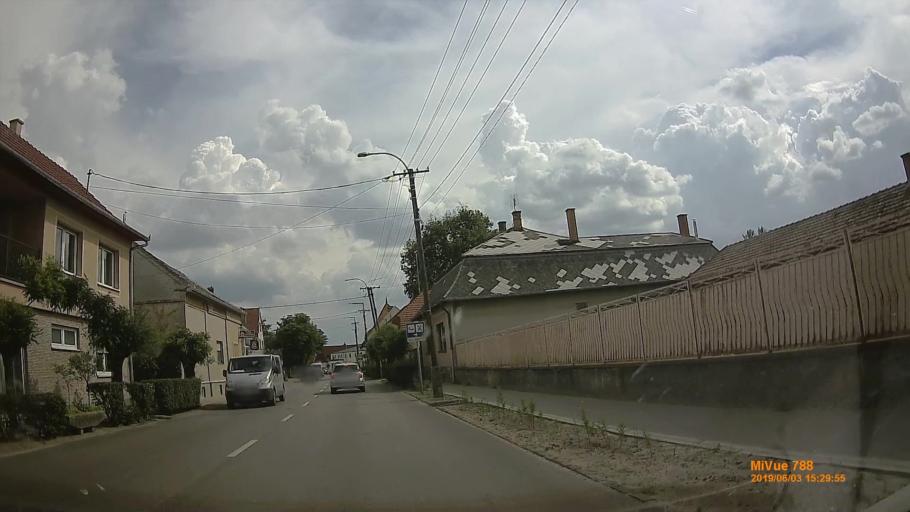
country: HU
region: Bacs-Kiskun
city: Soltvadkert
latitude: 46.5824
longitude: 19.3937
